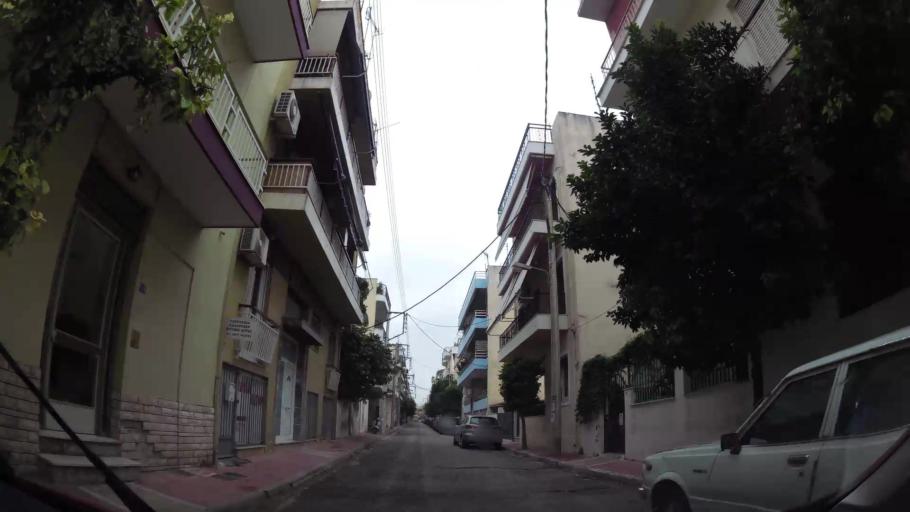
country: GR
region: Attica
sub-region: Nomarchia Athinas
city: Agioi Anargyroi
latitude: 38.0199
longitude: 23.7158
